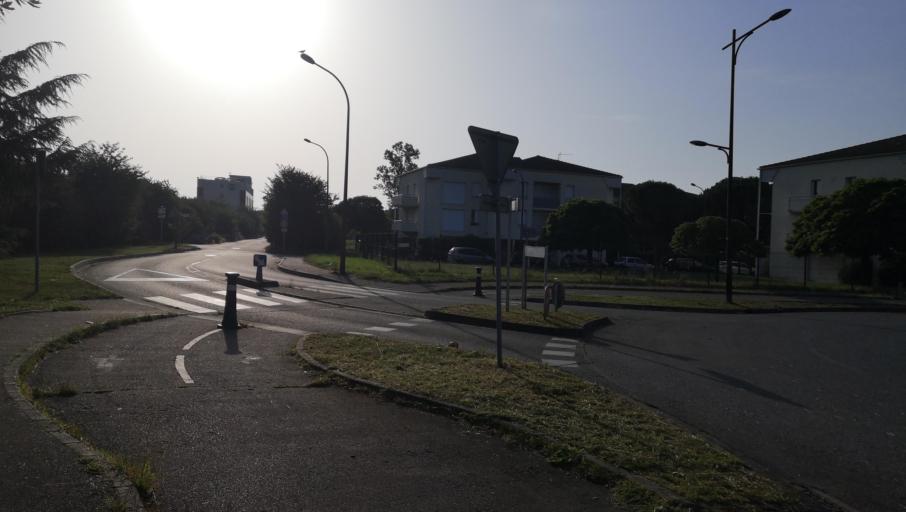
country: FR
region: Midi-Pyrenees
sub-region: Departement de la Haute-Garonne
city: Blagnac
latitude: 43.5988
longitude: 1.3930
